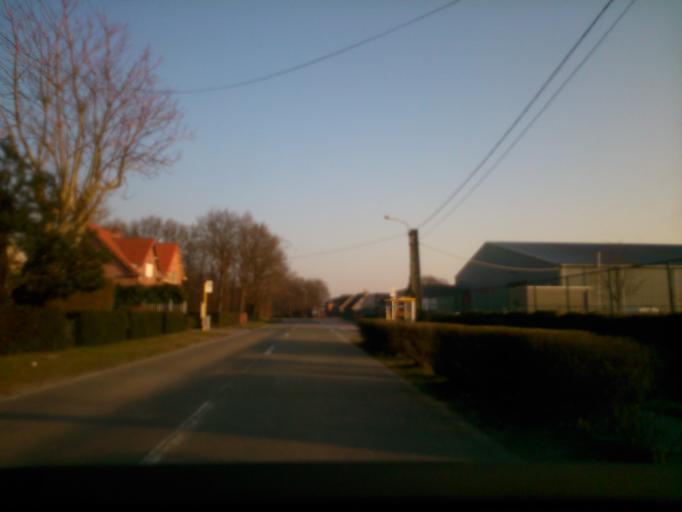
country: BE
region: Flanders
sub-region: Provincie Antwerpen
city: Stabroek
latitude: 51.3376
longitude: 4.3545
